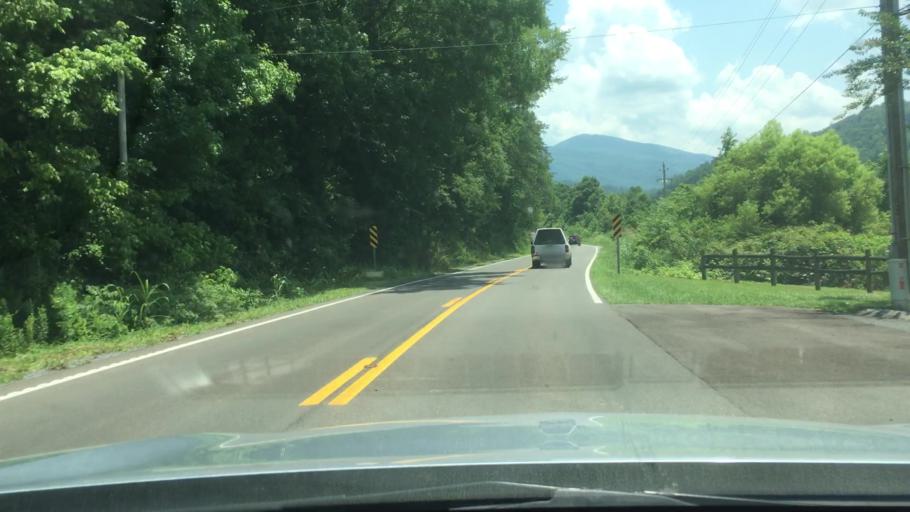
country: US
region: Tennessee
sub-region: Cocke County
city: Newport
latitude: 35.9181
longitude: -82.9894
